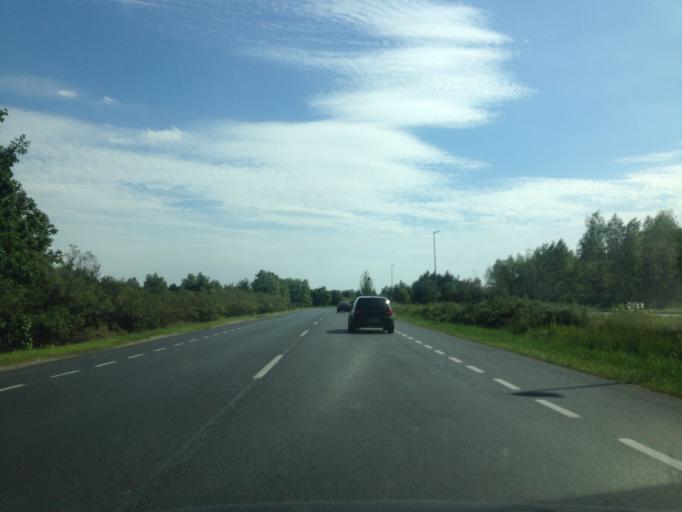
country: PL
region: Kujawsko-Pomorskie
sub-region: Torun
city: Torun
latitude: 53.0468
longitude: 18.6163
